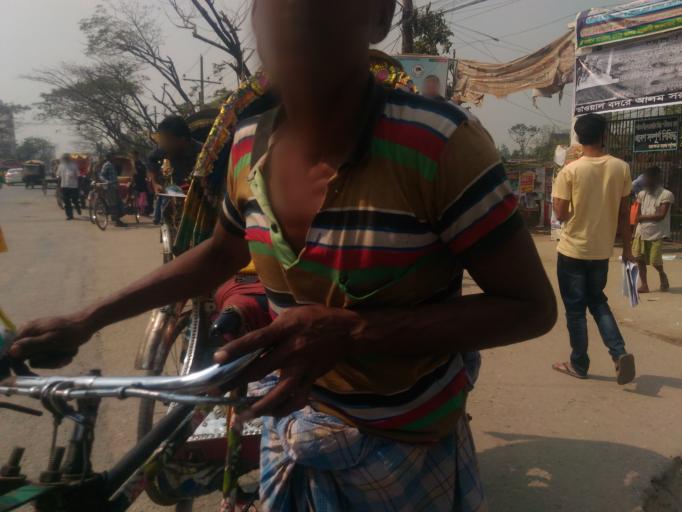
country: BD
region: Dhaka
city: Tungi
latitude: 23.9897
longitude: 90.3737
